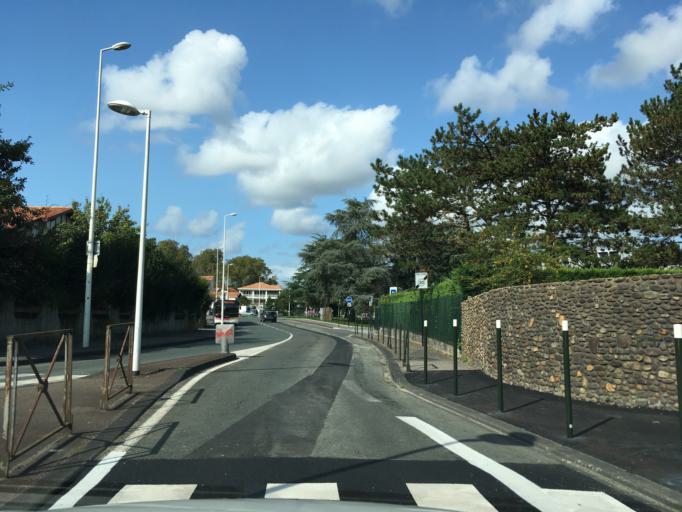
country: FR
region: Aquitaine
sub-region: Departement des Pyrenees-Atlantiques
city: Bayonne
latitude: 43.4831
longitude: -1.4767
